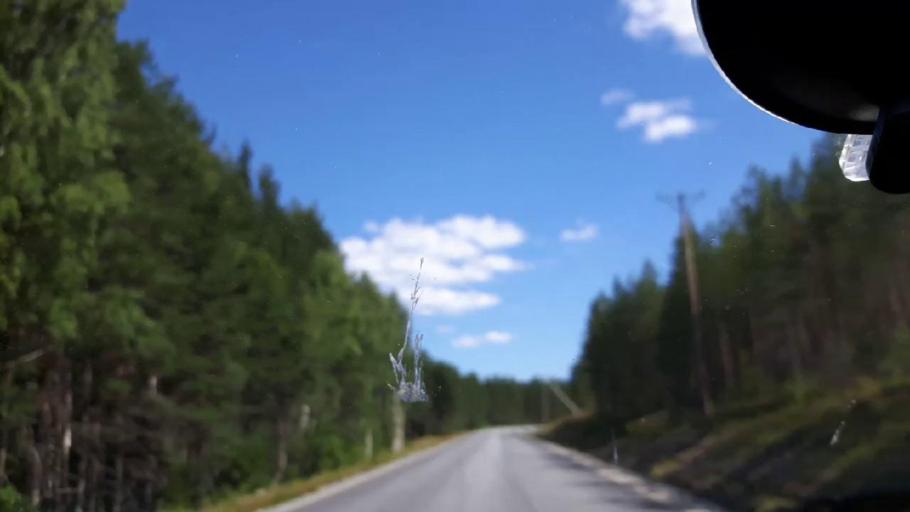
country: SE
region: Vaesternorrland
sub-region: Ange Kommun
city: Fransta
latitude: 62.7010
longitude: 16.3844
